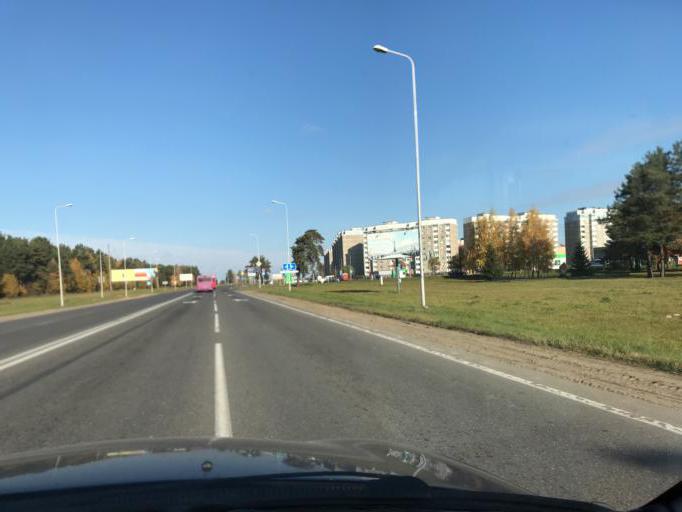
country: BY
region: Grodnenskaya
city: Lida
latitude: 53.8904
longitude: 25.2527
